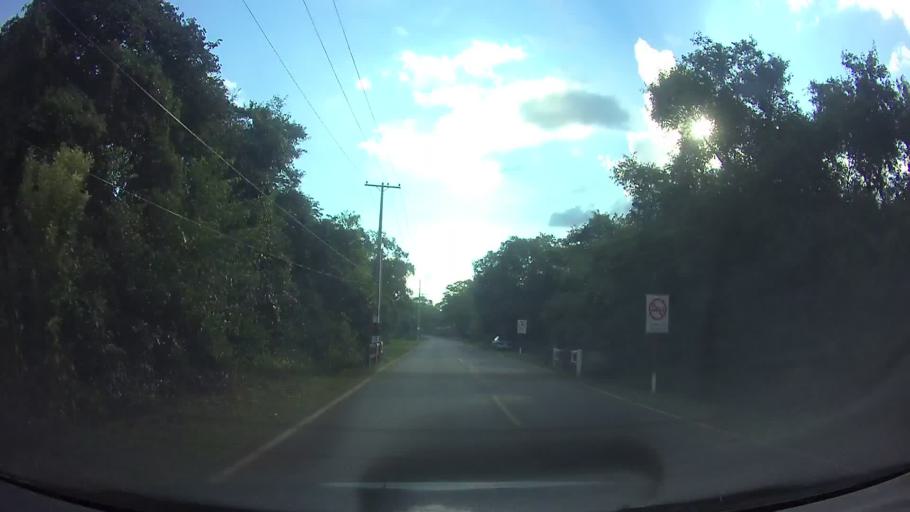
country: PY
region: Central
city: Aregua
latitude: -25.2714
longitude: -57.4293
